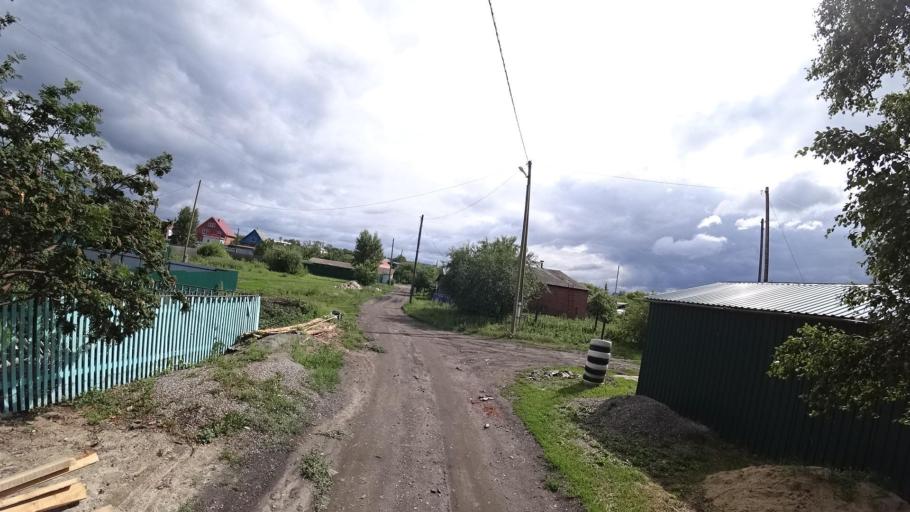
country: RU
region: Sverdlovsk
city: Kamyshlov
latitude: 56.8600
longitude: 62.7108
